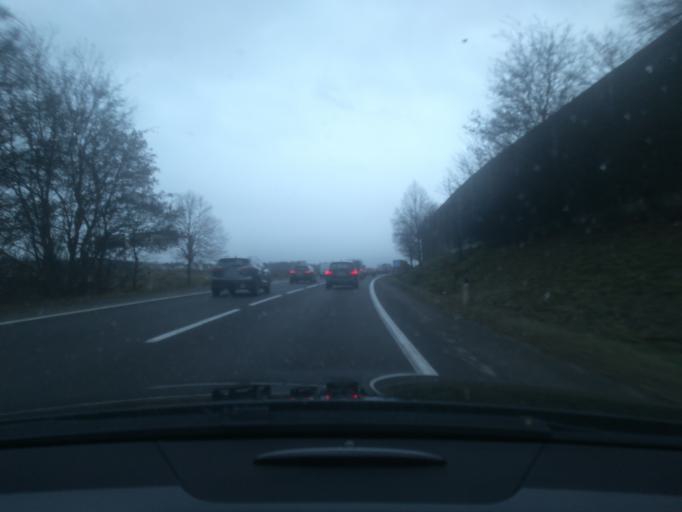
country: AT
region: Upper Austria
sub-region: Politischer Bezirk Linz-Land
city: Ansfelden
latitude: 48.2211
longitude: 14.2974
